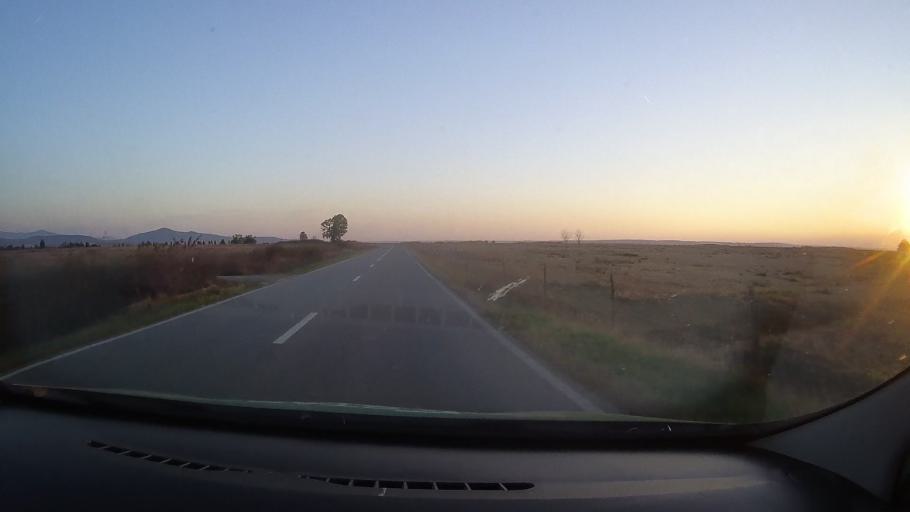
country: RO
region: Timis
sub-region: Comuna Manastiur
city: Manastiur
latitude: 45.8221
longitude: 22.0708
